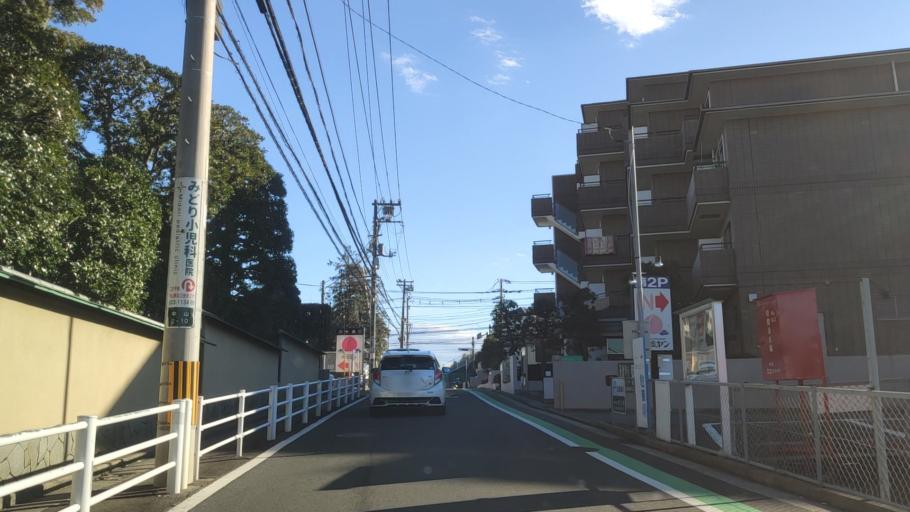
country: JP
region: Tokyo
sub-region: Machida-shi
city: Machida
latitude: 35.5136
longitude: 139.5481
